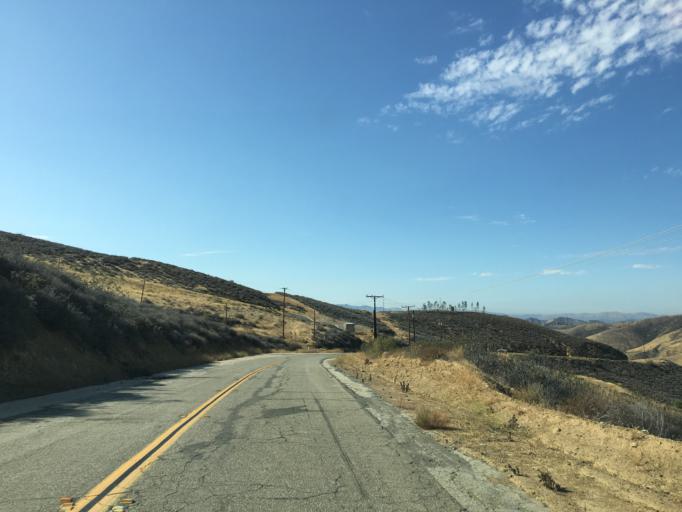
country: US
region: California
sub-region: Los Angeles County
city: Castaic
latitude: 34.5605
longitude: -118.6576
